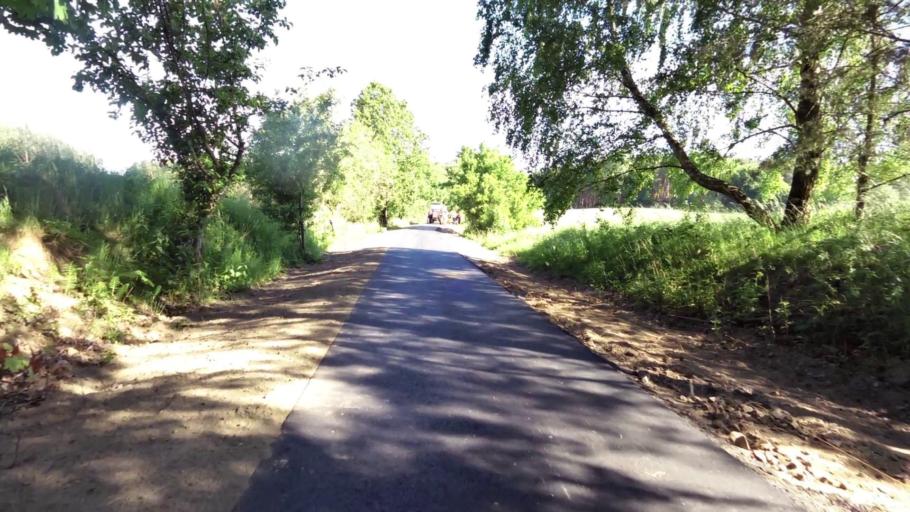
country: PL
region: West Pomeranian Voivodeship
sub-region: Powiat gryfinski
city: Banie
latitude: 53.1976
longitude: 14.6187
